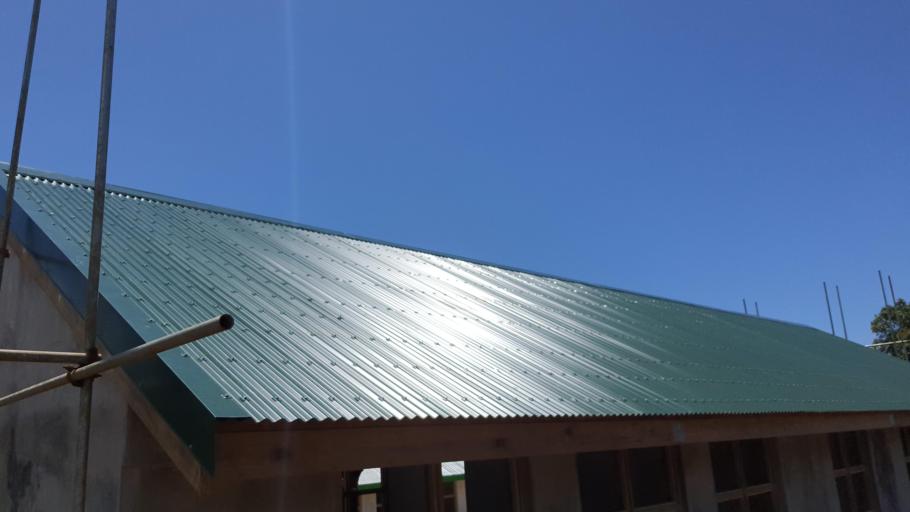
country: VU
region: Malampa
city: Lakatoro
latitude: -16.4998
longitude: 167.6498
